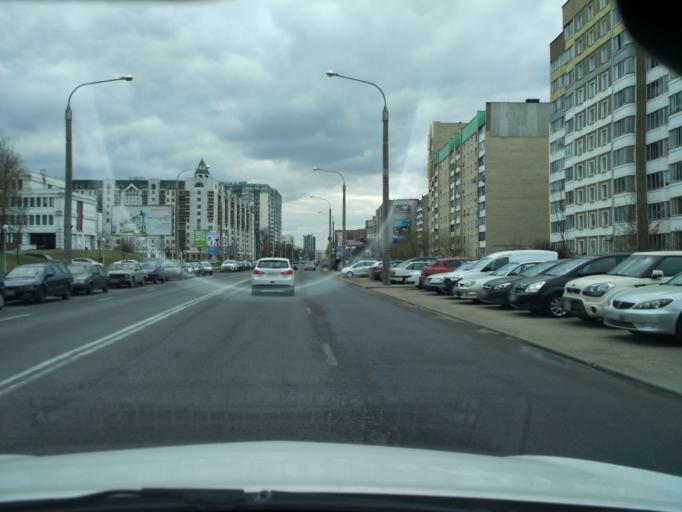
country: BY
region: Minsk
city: Minsk
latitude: 53.9347
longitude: 27.5916
